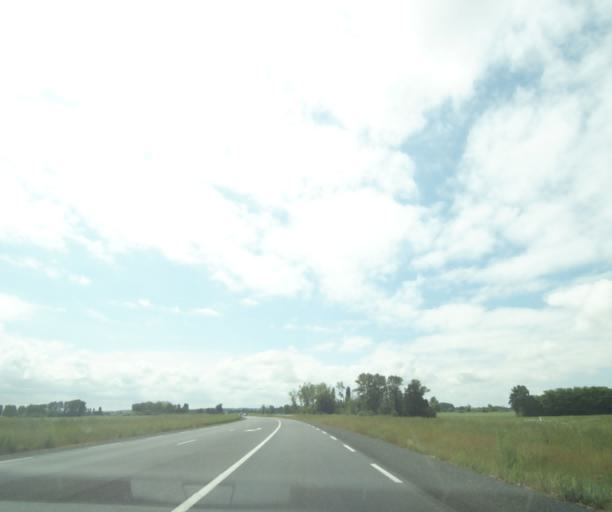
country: FR
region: Poitou-Charentes
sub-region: Departement des Deux-Sevres
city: Sainte-Verge
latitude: 47.0243
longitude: -0.2026
